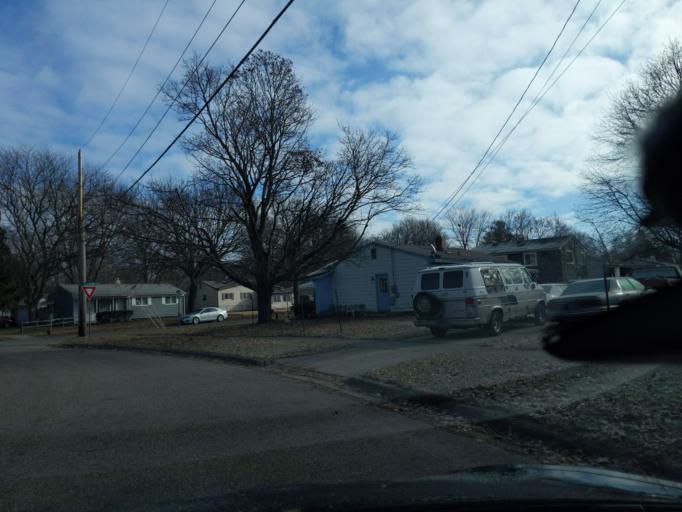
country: US
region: Michigan
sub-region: Eaton County
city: Waverly
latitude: 42.6919
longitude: -84.5999
